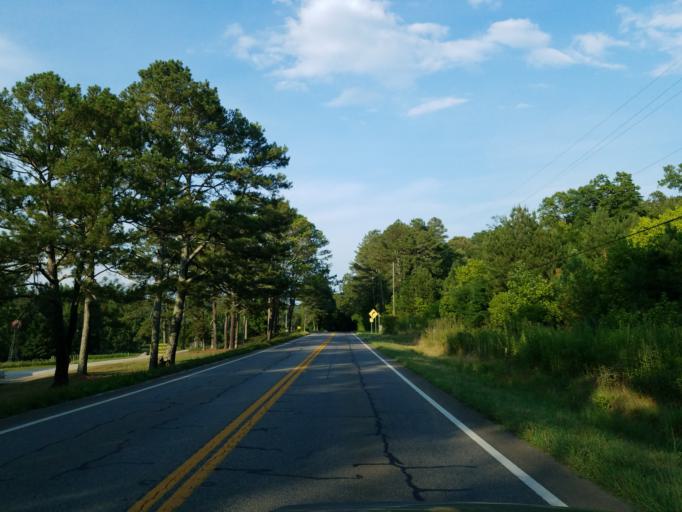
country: US
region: Georgia
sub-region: Pickens County
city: Jasper
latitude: 34.5202
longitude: -84.5302
